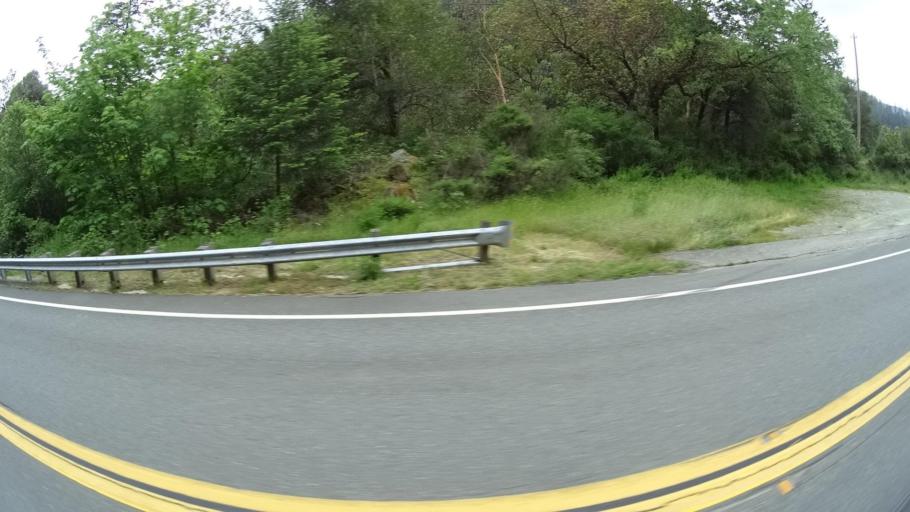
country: US
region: California
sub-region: Humboldt County
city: Willow Creek
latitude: 41.1116
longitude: -123.6863
